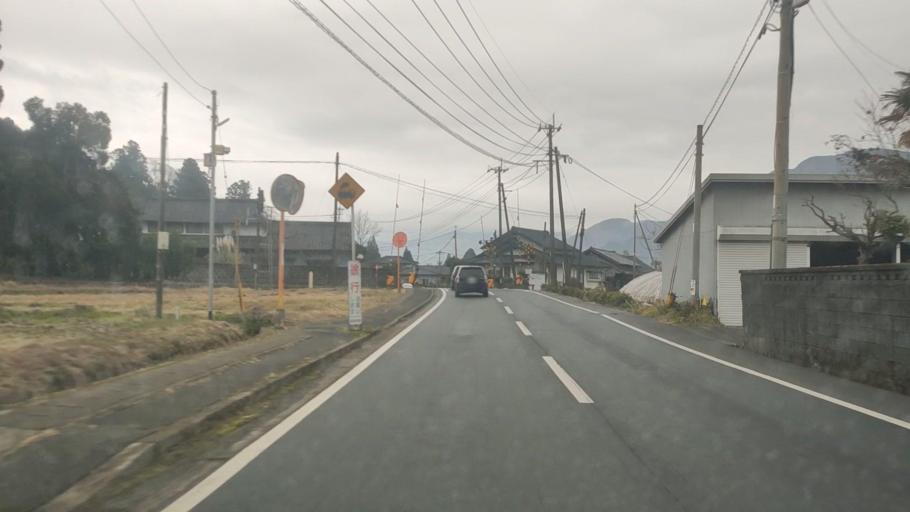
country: JP
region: Kumamoto
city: Aso
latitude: 32.9209
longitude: 130.9938
